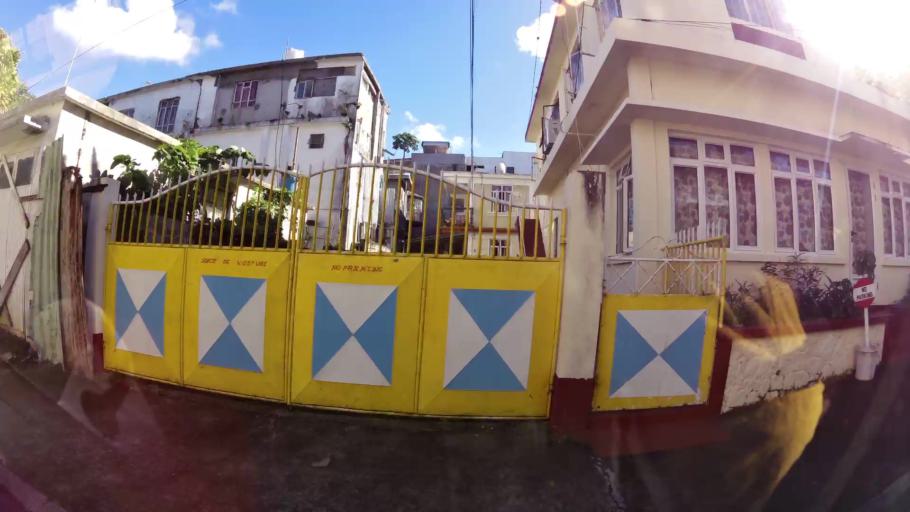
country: MU
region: Grand Port
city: Mahebourg
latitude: -20.4102
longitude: 57.7098
